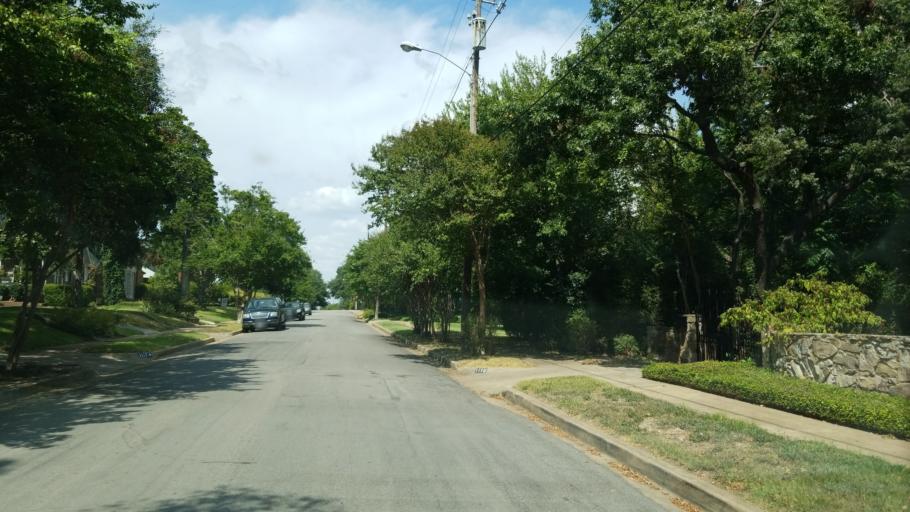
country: US
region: Texas
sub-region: Dallas County
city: Dallas
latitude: 32.7578
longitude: -96.8391
